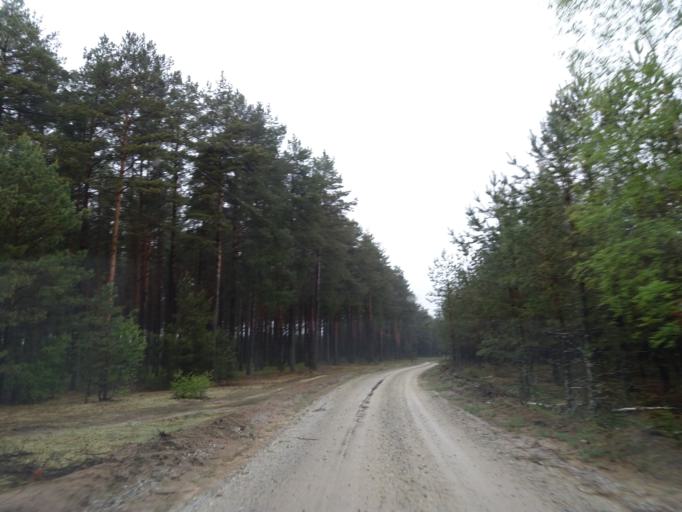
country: PL
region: West Pomeranian Voivodeship
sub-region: Powiat drawski
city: Kalisz Pomorski
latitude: 53.1872
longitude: 15.9729
